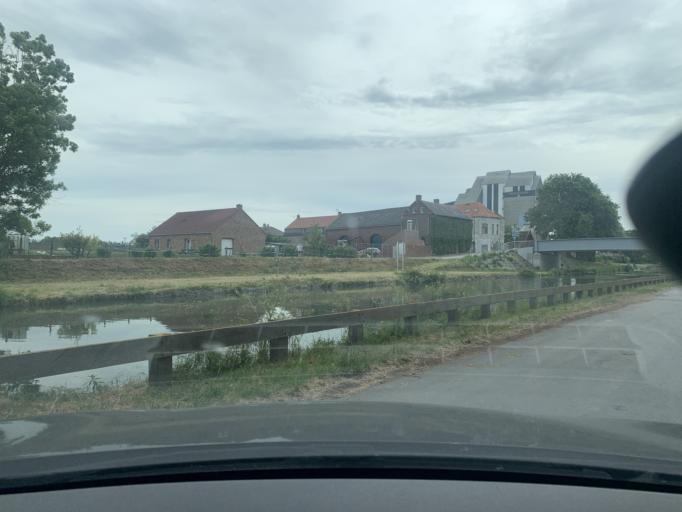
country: FR
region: Nord-Pas-de-Calais
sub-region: Departement du Nord
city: Marcoing
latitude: 50.1417
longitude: 3.1877
